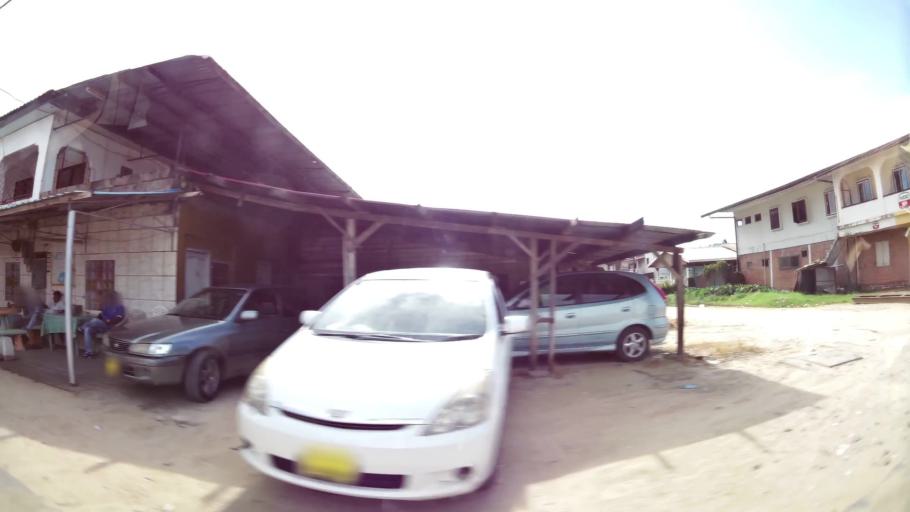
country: SR
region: Paramaribo
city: Paramaribo
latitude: 5.8464
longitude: -55.1546
